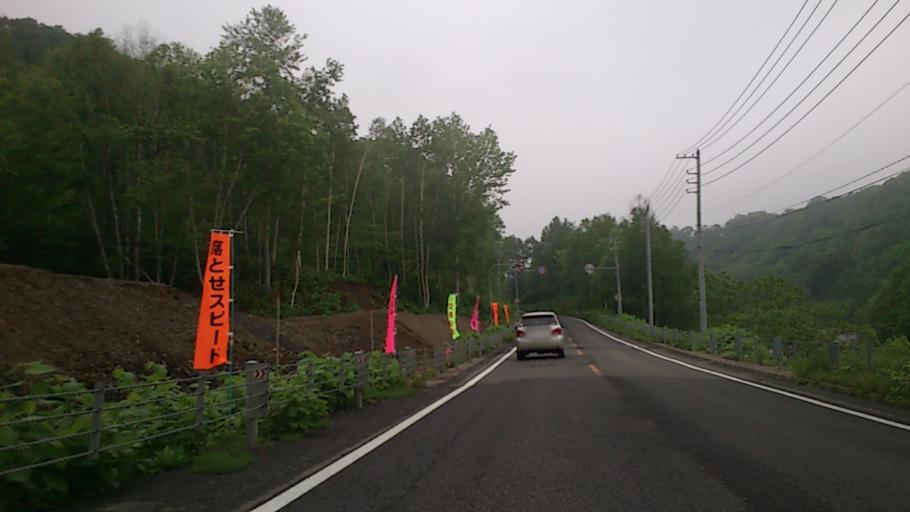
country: JP
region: Hokkaido
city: Niseko Town
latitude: 42.8640
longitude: 140.8581
